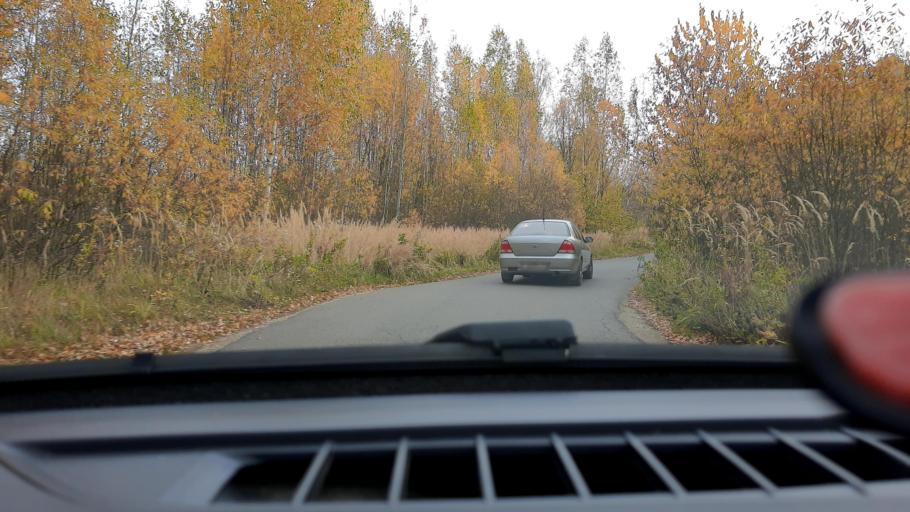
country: RU
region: Nizjnij Novgorod
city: Gorbatovka
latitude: 56.2908
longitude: 43.8304
